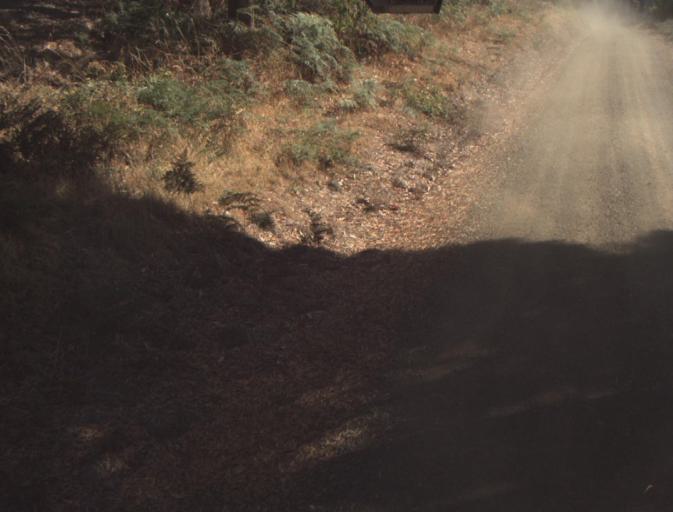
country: AU
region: Tasmania
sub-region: Launceston
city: Mayfield
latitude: -41.1633
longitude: 147.2112
